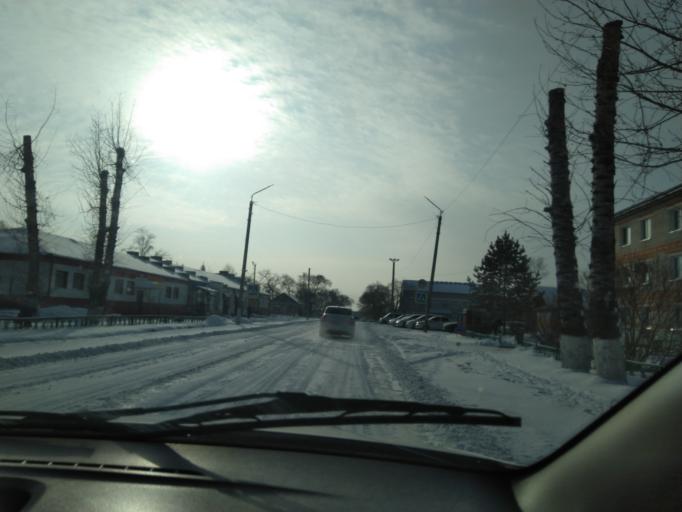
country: RU
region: Amur
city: Poyarkovo
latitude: 49.6219
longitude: 128.6511
